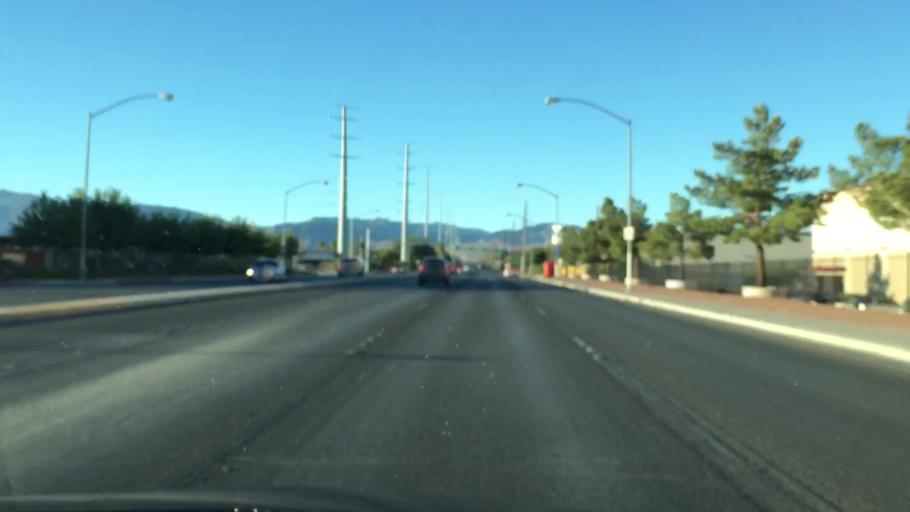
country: US
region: Nevada
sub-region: Clark County
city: Nellis Air Force Base
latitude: 36.2386
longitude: -115.0800
